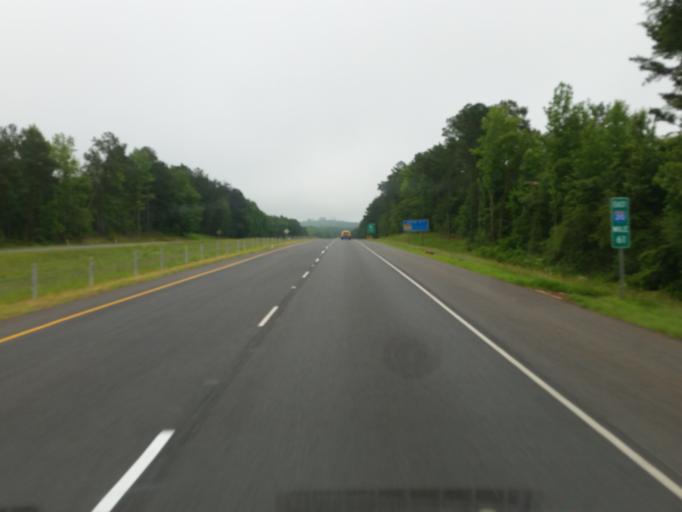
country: US
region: Louisiana
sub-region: Bienville Parish
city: Arcadia
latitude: 32.5633
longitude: -93.0621
